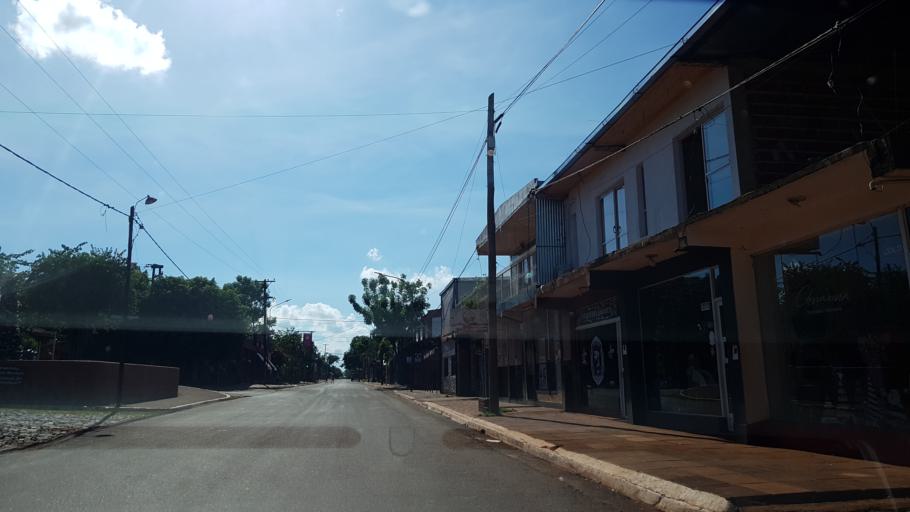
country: AR
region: Misiones
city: Puerto Libertad
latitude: -25.9212
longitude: -54.5809
